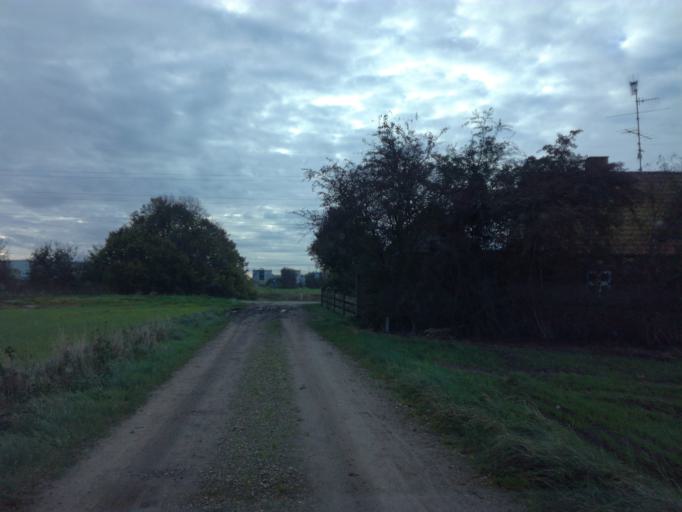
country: DK
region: South Denmark
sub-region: Fredericia Kommune
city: Fredericia
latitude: 55.6006
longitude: 9.7467
